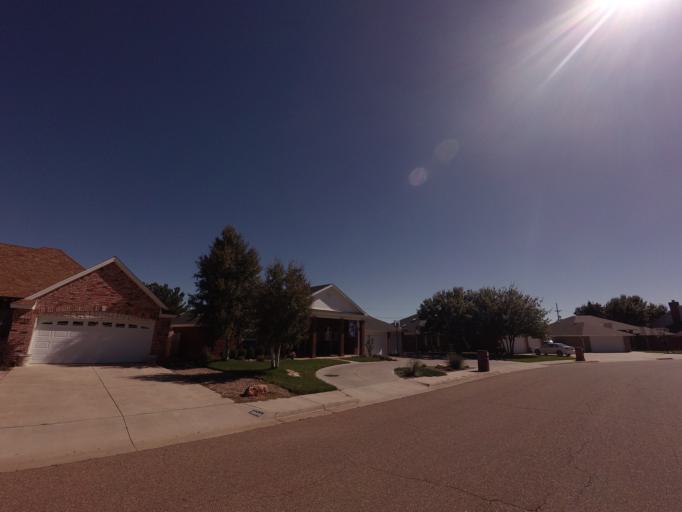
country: US
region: New Mexico
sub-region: Curry County
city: Clovis
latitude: 34.4255
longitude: -103.1706
